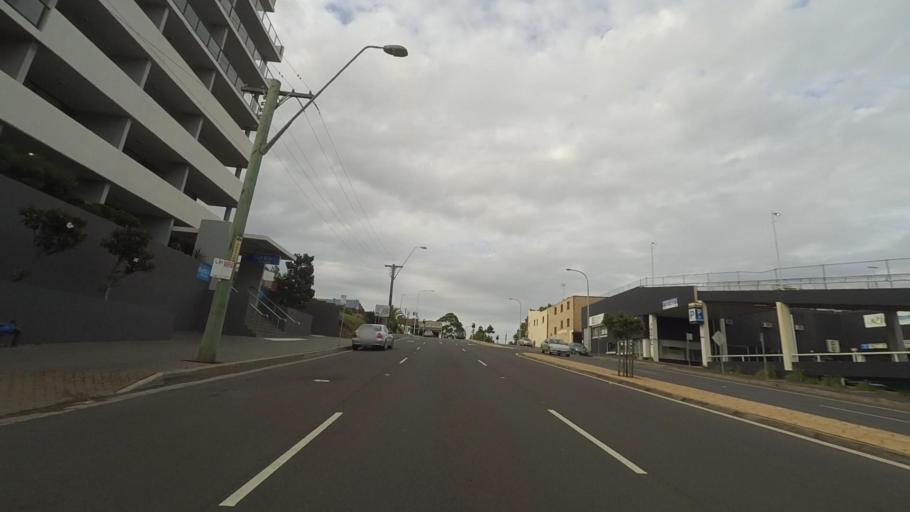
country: AU
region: New South Wales
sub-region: Wollongong
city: Wollongong
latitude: -34.4268
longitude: 150.8871
